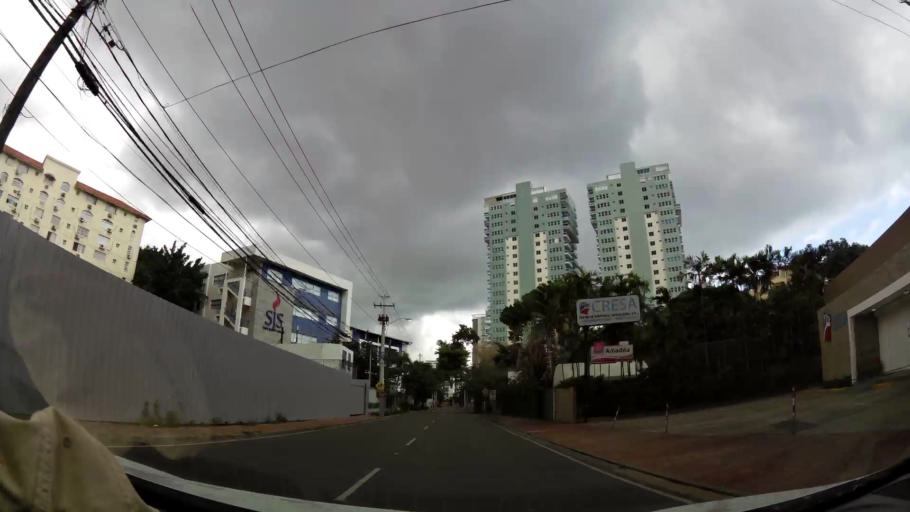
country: DO
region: Nacional
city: La Julia
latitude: 18.4699
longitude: -69.9173
